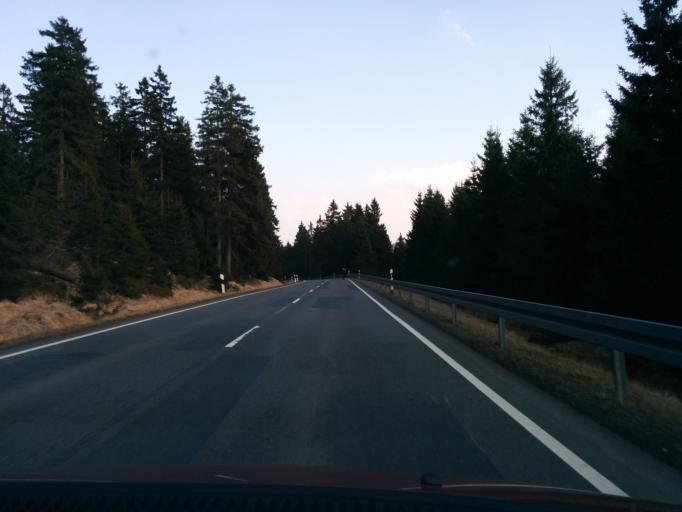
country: DE
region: Lower Saxony
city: Altenau
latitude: 51.7674
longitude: 10.4721
